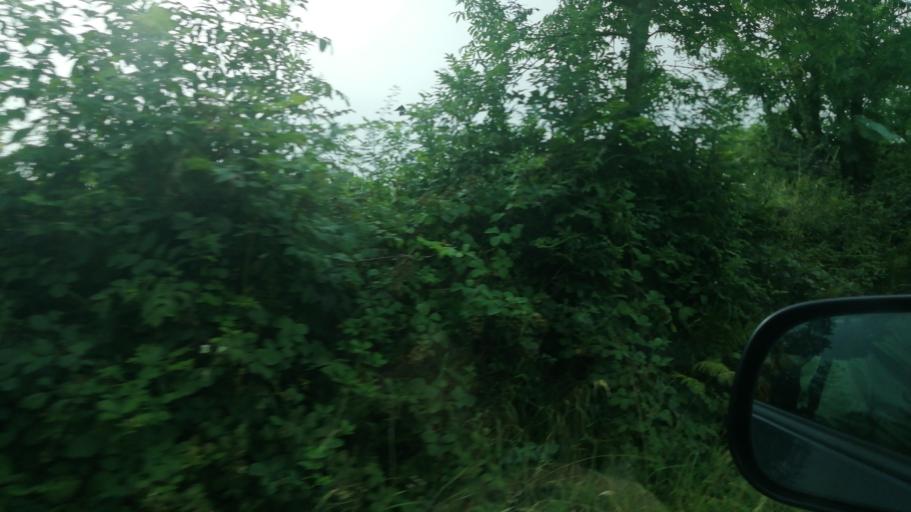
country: IE
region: Munster
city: Fethard
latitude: 52.5776
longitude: -7.6432
